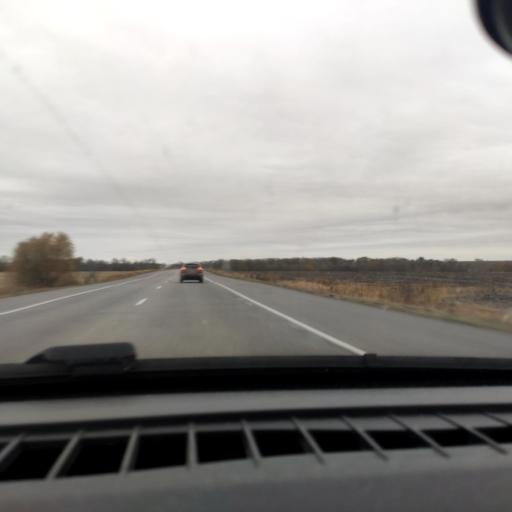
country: RU
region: Voronezj
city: Devitsa
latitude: 51.5839
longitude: 38.9763
